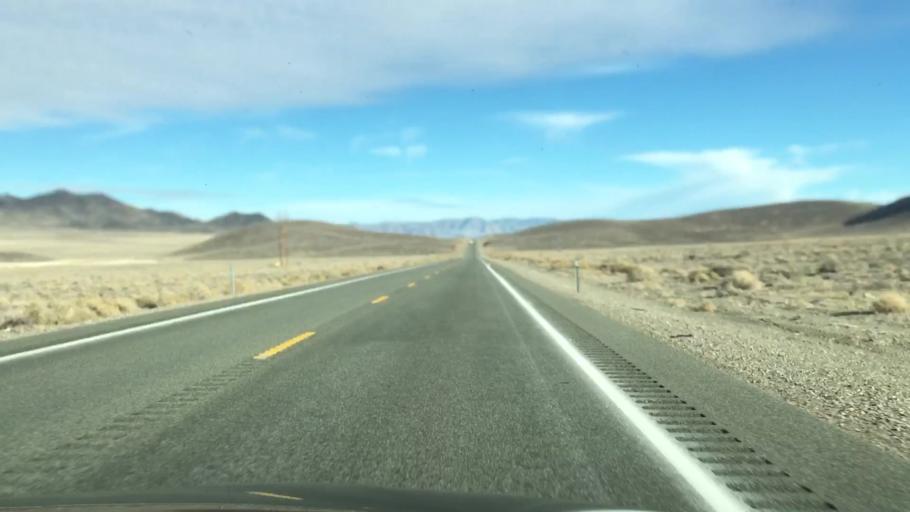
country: US
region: Nevada
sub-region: Mineral County
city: Hawthorne
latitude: 38.5500
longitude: -118.4562
